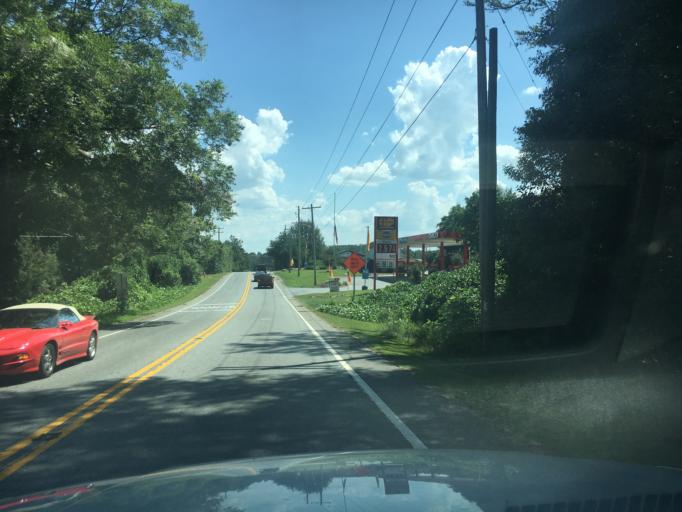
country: US
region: North Carolina
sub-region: Rutherford County
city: Forest City
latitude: 35.3057
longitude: -81.8580
